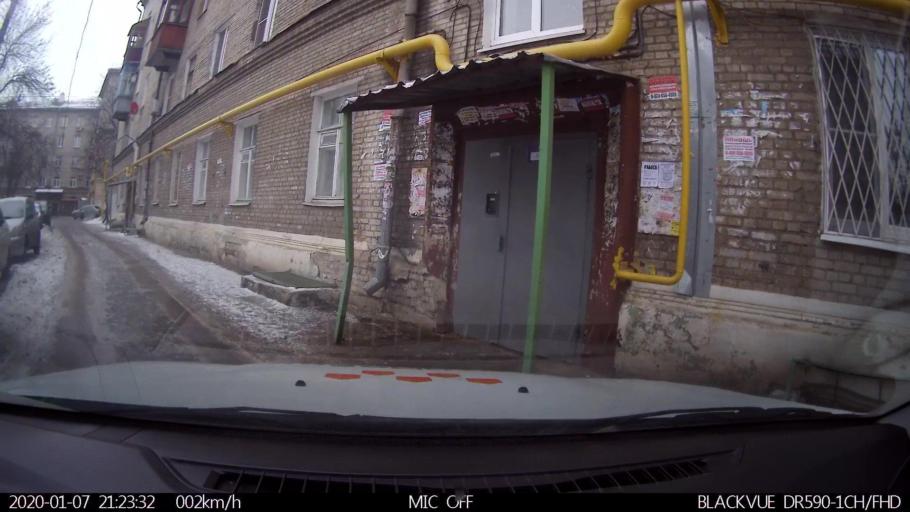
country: RU
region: Nizjnij Novgorod
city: Nizhniy Novgorod
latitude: 56.3149
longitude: 43.8728
